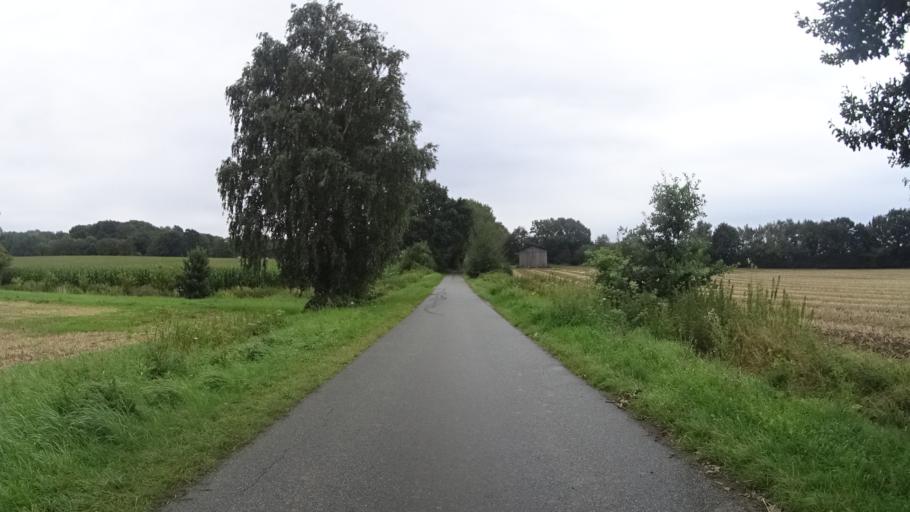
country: DE
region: Schleswig-Holstein
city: Lasbek
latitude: 53.7280
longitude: 10.3863
